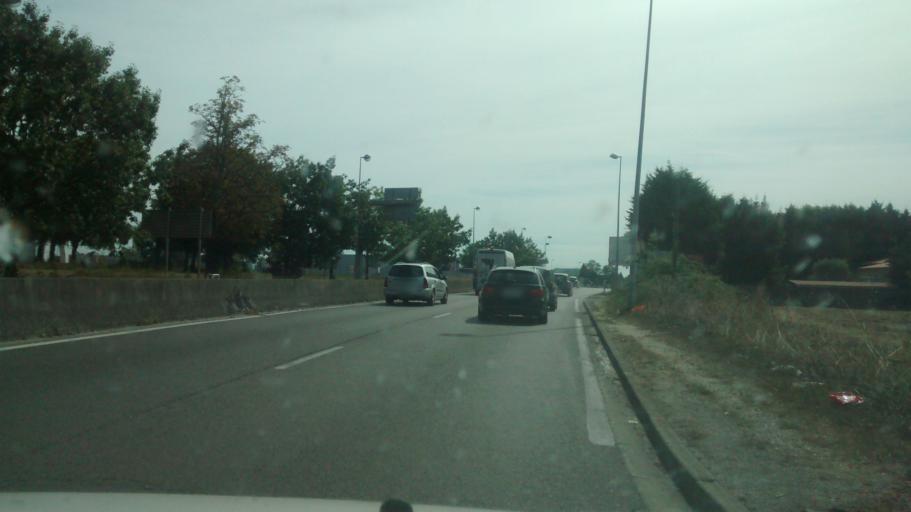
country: FR
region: Aquitaine
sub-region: Departement de la Gironde
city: Floirac
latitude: 44.8426
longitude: -0.4994
